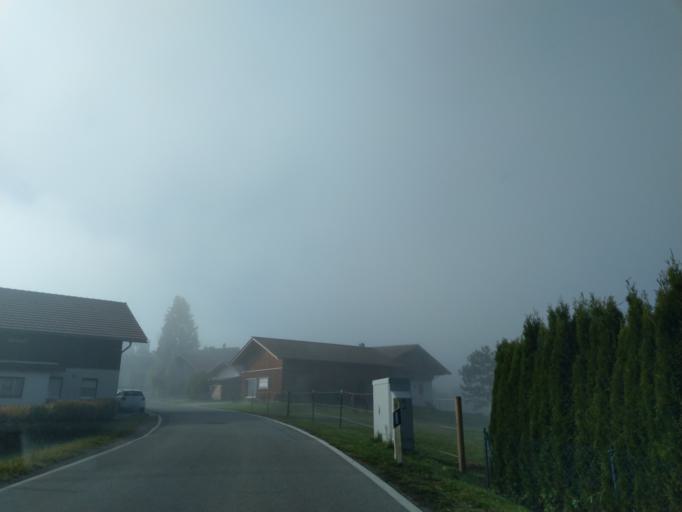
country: DE
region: Bavaria
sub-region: Lower Bavaria
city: Aussernzell
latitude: 48.7192
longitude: 13.2016
